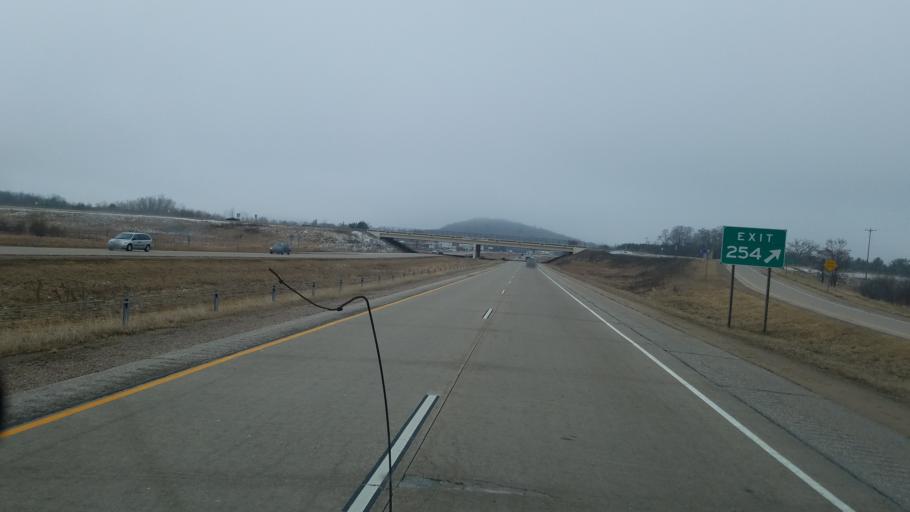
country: US
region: Wisconsin
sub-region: Waupaca County
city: Waupaca
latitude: 44.3298
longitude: -89.0380
